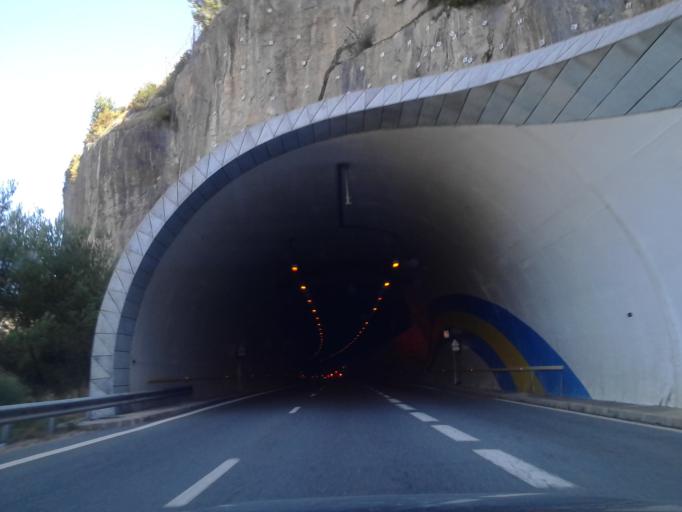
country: FR
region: Languedoc-Roussillon
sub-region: Departement de l'Herault
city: Lodeve
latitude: 43.8271
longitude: 3.3163
